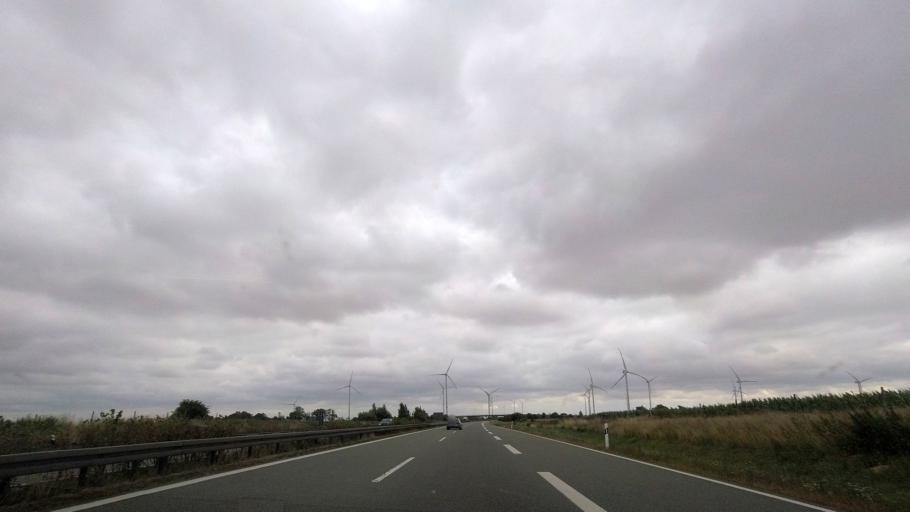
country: DE
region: Mecklenburg-Vorpommern
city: Dersekow
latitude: 54.0706
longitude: 13.2141
